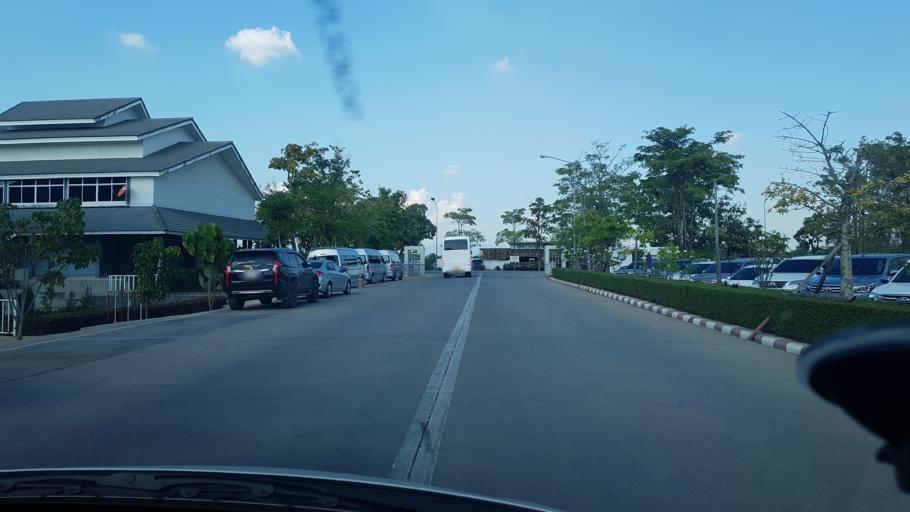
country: TH
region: Chiang Rai
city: Mae Lao
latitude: 19.8242
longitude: 99.7615
